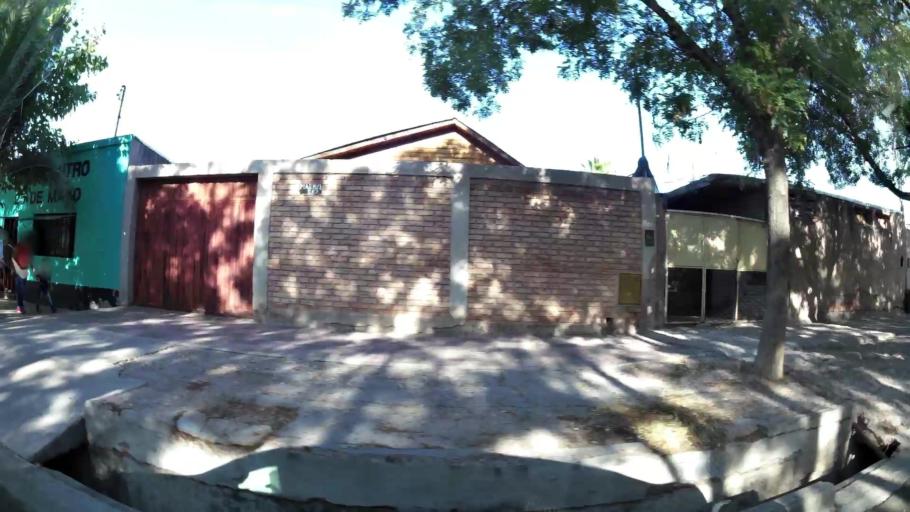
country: AR
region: Mendoza
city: Mendoza
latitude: -32.9028
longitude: -68.8211
